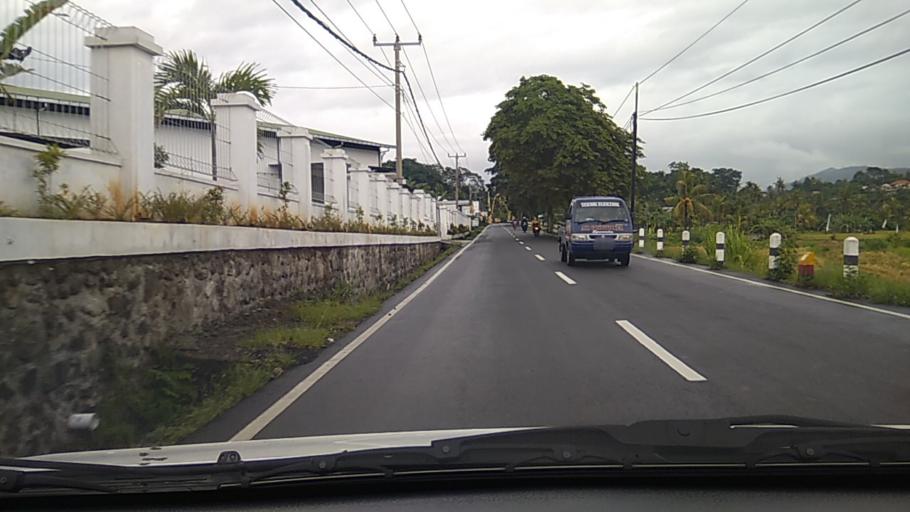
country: ID
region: Bali
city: Banjar Budakeling
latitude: -8.4283
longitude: 115.5923
